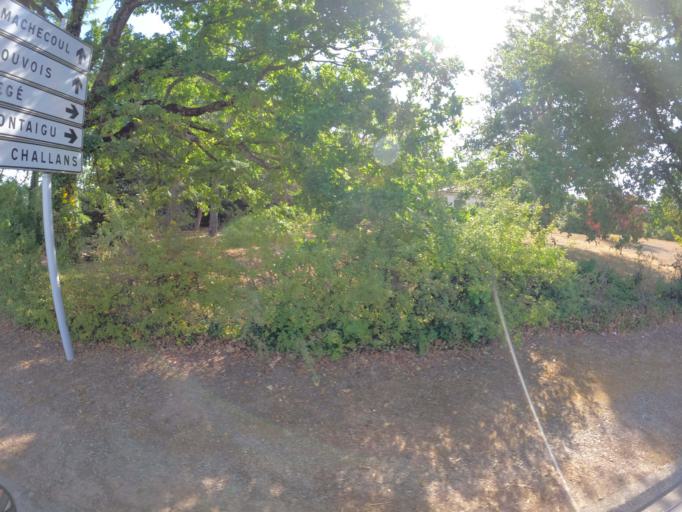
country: FR
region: Pays de la Loire
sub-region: Departement de la Vendee
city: Falleron
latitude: 46.8792
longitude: -1.7037
